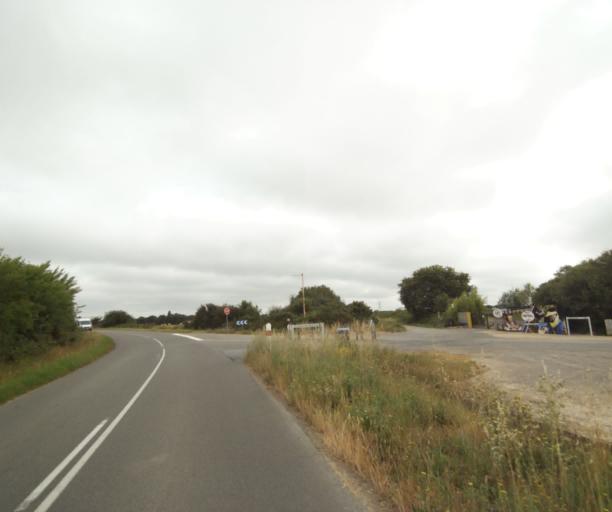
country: FR
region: Pays de la Loire
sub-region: Departement de la Vendee
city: Sainte-Foy
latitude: 46.5090
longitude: -1.6864
